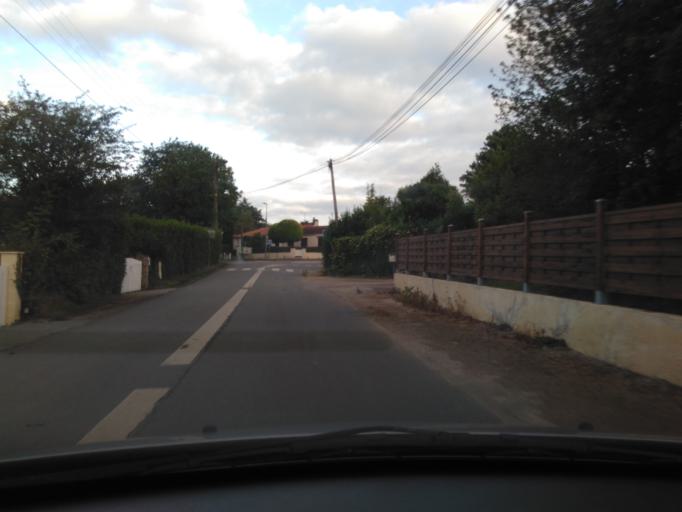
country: FR
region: Pays de la Loire
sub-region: Departement de la Vendee
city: Dompierre-sur-Yon
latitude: 46.7331
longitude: -1.3950
